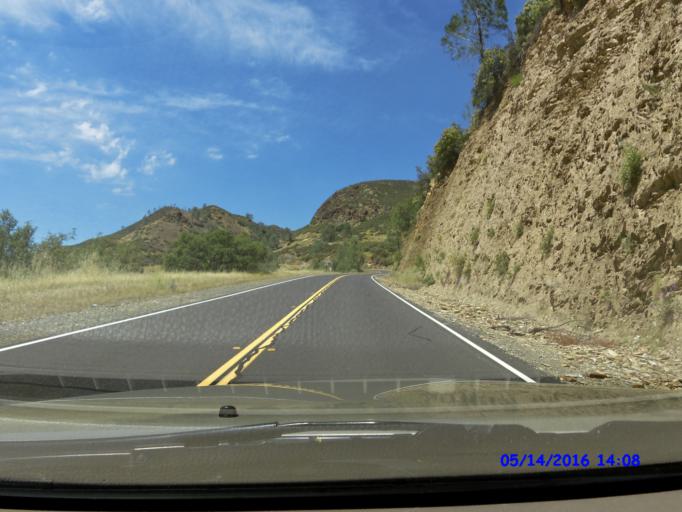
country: US
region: California
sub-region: Mariposa County
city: Mariposa
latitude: 37.6173
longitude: -120.1413
